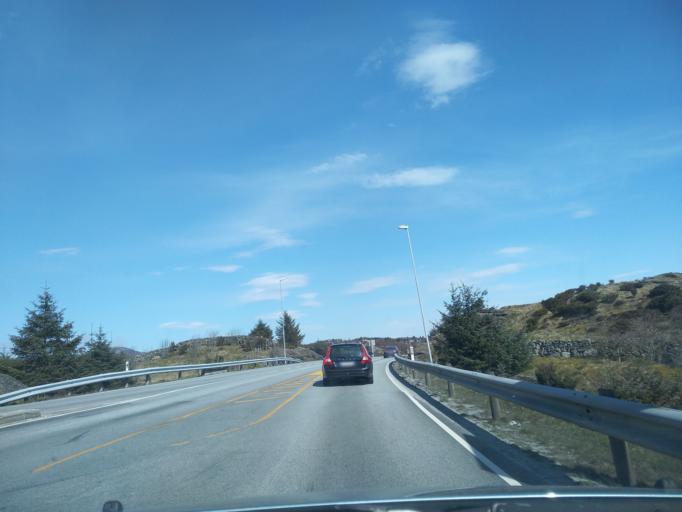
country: NO
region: Rogaland
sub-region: Bokn
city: Bokn
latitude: 59.1718
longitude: 5.4503
